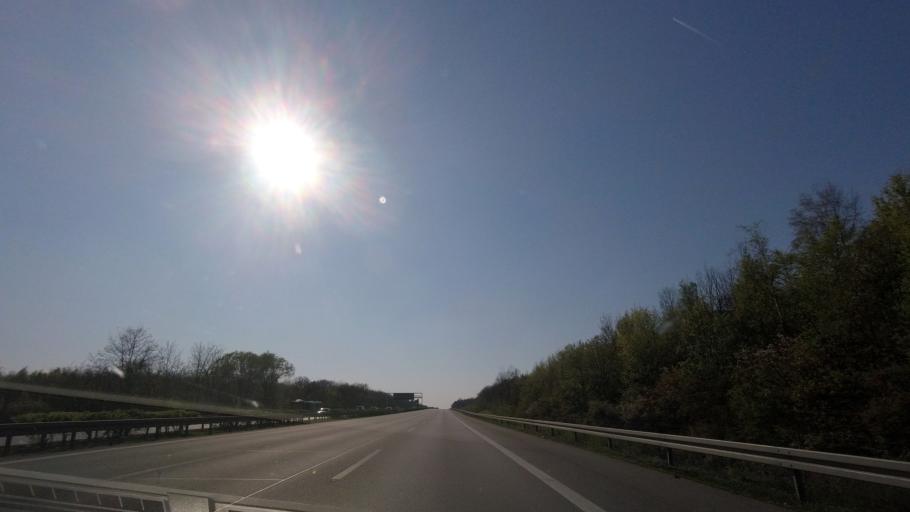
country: DE
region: Brandenburg
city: Rangsdorf
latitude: 52.3062
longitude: 13.4352
